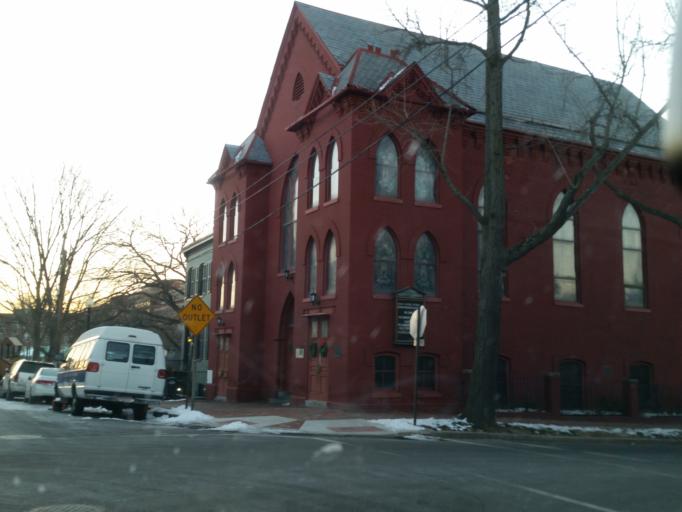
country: US
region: Washington, D.C.
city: Washington, D.C.
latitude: 38.9077
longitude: -77.0559
